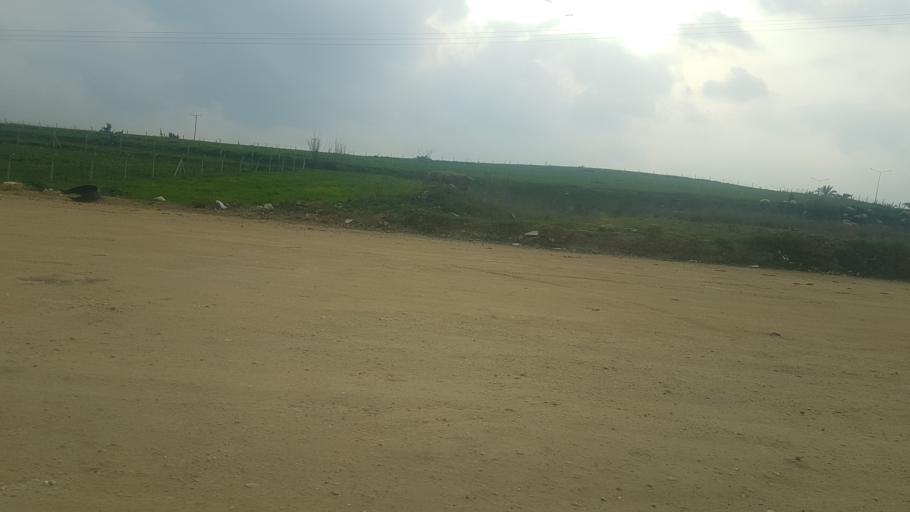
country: TR
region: Adana
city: Seyhan
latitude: 37.0510
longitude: 35.2088
